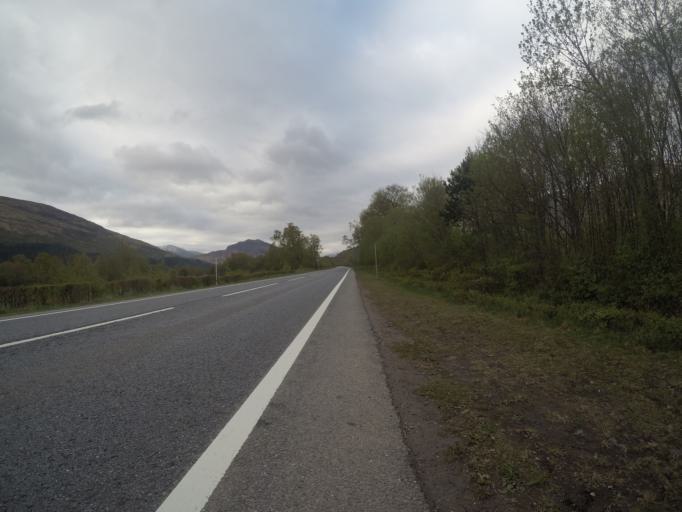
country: GB
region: Scotland
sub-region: Highland
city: Spean Bridge
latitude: 56.9513
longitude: -4.4956
